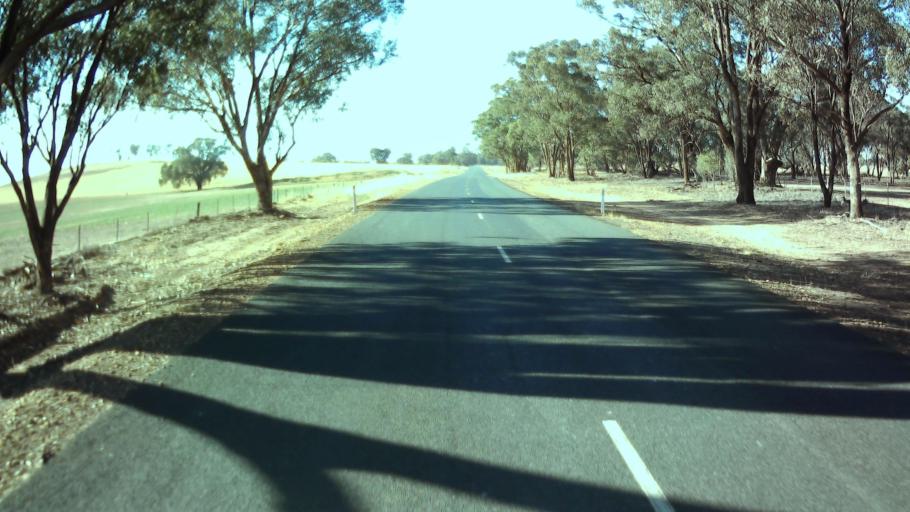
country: AU
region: New South Wales
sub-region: Weddin
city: Grenfell
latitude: -33.9673
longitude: 148.1408
